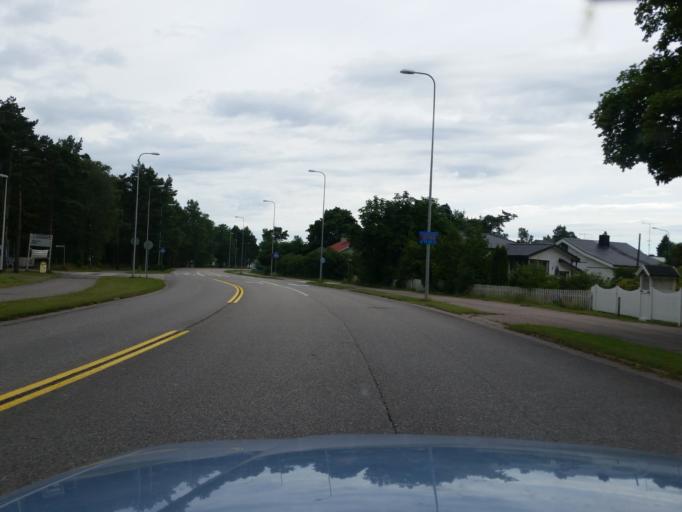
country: FI
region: Uusimaa
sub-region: Raaseporin
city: Hanko
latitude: 59.8354
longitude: 22.9913
